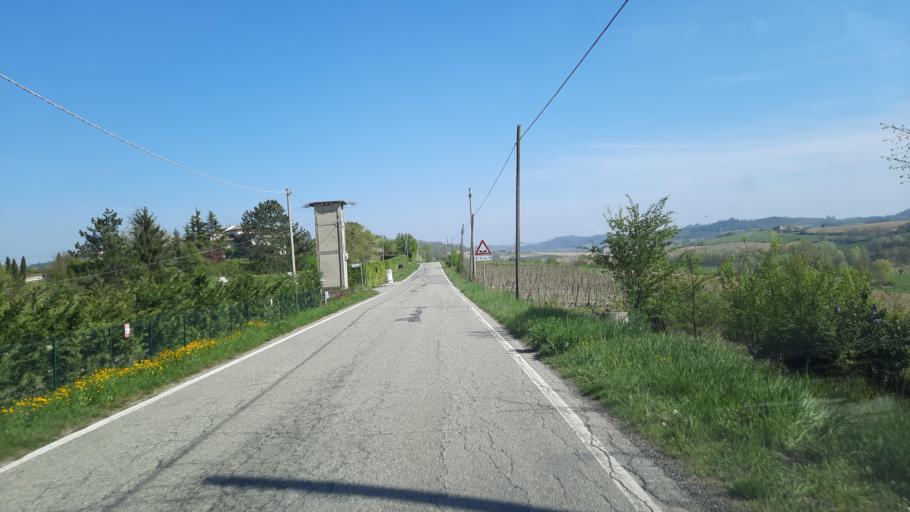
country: IT
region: Piedmont
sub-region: Provincia di Alessandria
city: Altavilla Monferrato
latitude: 45.0145
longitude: 8.3683
